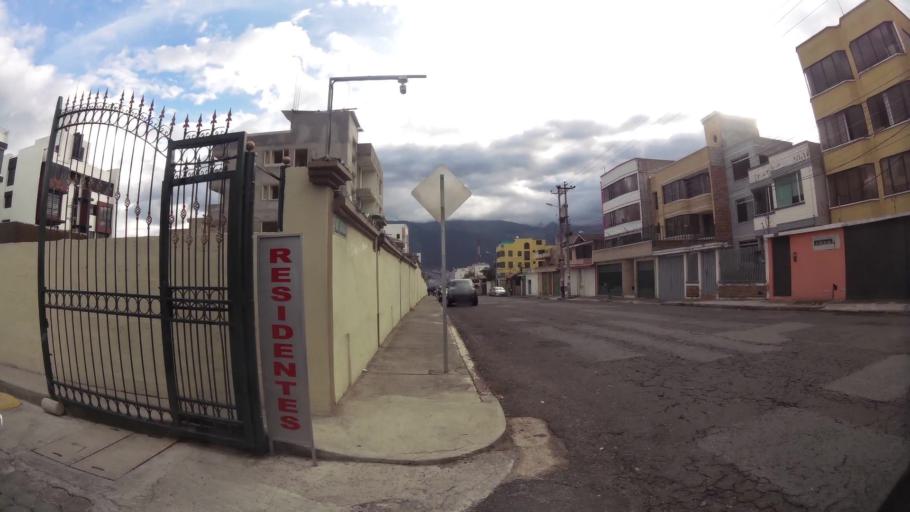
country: EC
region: Pichincha
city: Quito
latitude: -0.1364
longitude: -78.4633
